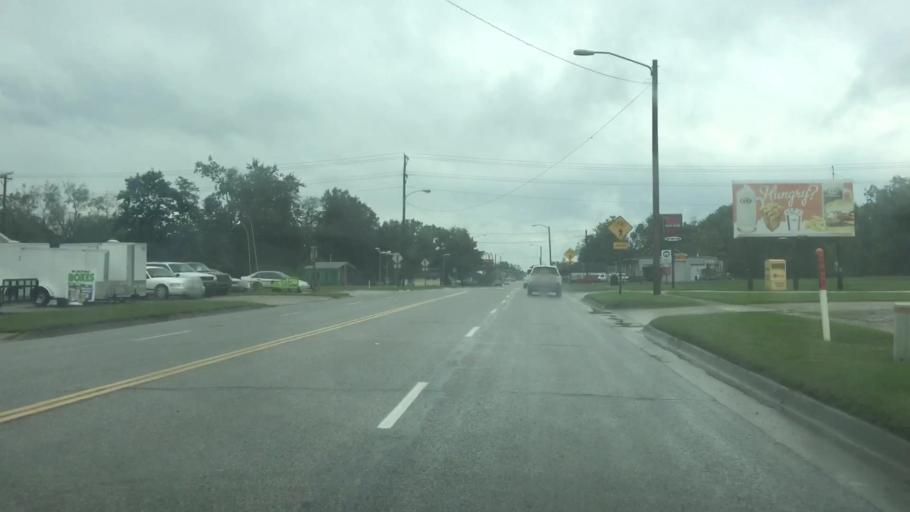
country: US
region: Kansas
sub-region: Allen County
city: Iola
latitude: 37.9263
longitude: -95.4091
